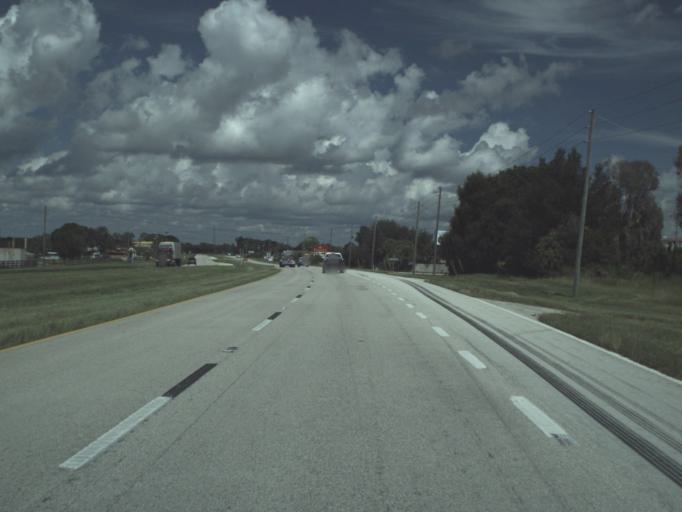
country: US
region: Florida
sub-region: Highlands County
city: Lake Placid
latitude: 27.2332
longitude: -81.3296
